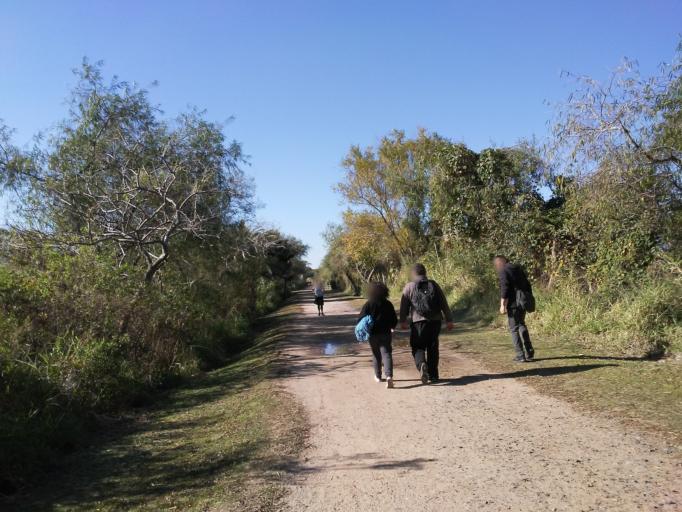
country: AR
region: Buenos Aires F.D.
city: Buenos Aires
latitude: -34.6087
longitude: -58.3557
